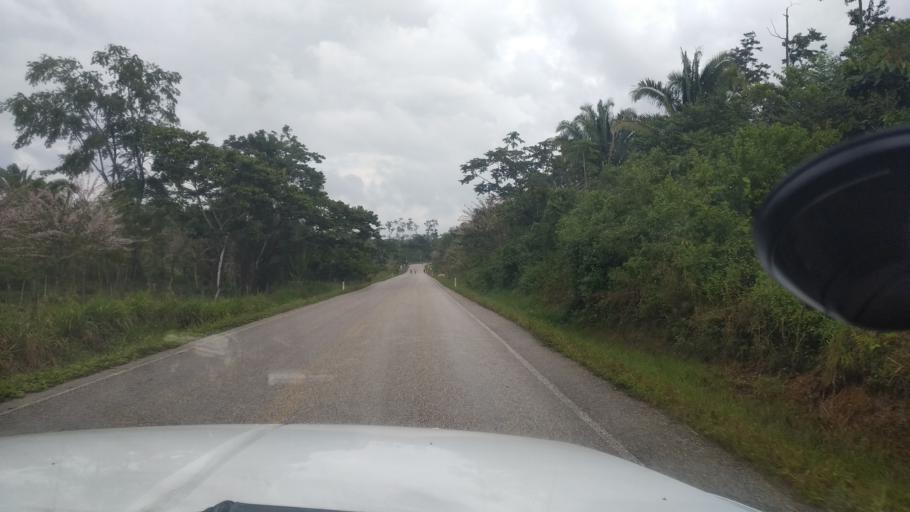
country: GT
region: Peten
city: San Luis
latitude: 16.1997
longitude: -89.1495
